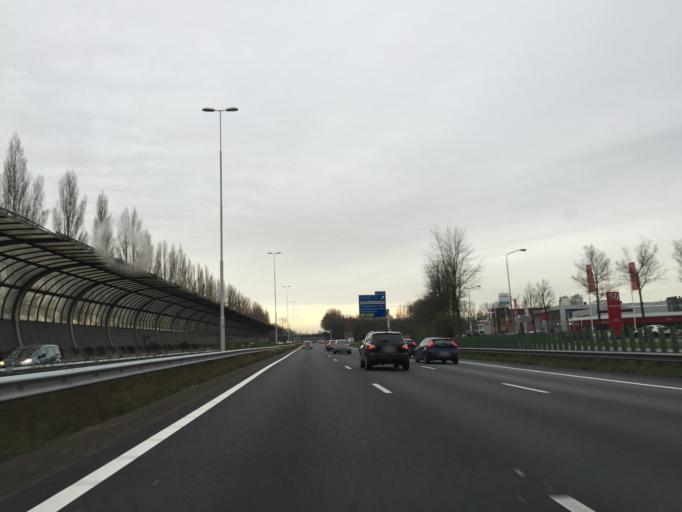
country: NL
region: South Holland
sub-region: Gemeente Zwijndrecht
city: Zwijndrecht
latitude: 51.7903
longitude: 4.6491
